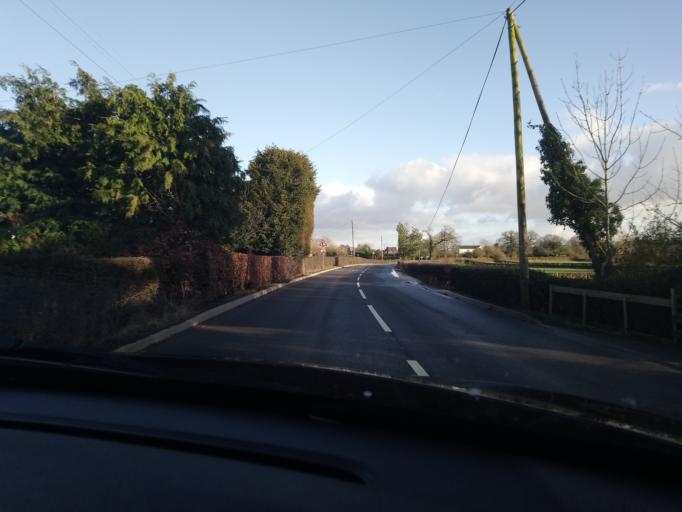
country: GB
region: Wales
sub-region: Wrexham
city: Overton
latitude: 52.9240
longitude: -2.9355
